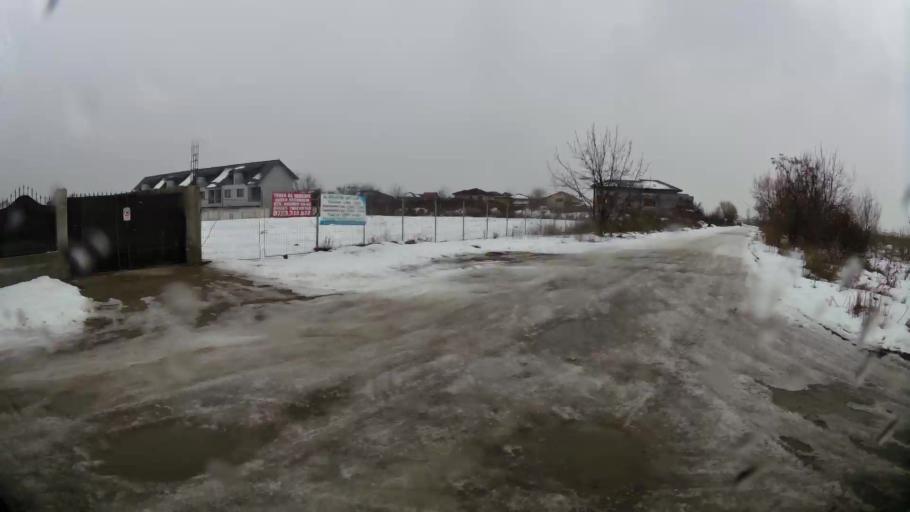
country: RO
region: Ilfov
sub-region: Comuna Chiajna
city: Rosu
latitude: 44.4032
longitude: 26.0140
